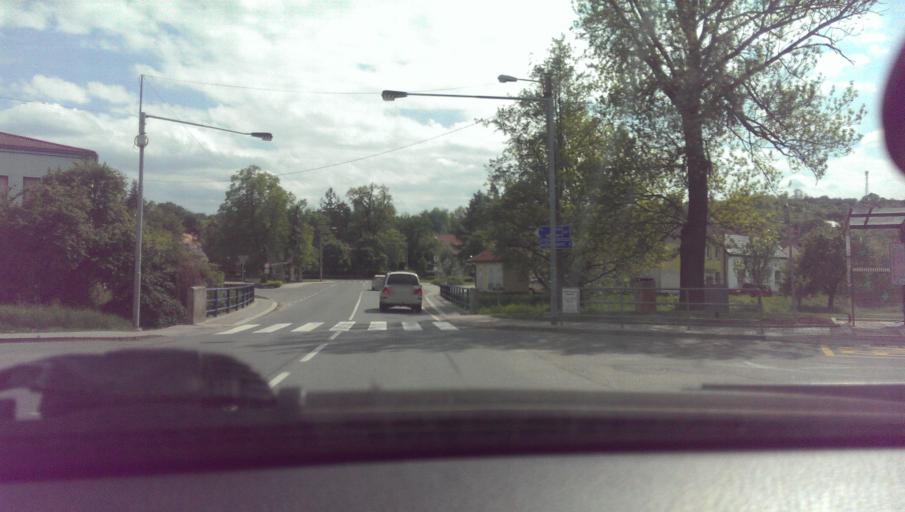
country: CZ
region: Zlin
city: Bilovice
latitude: 49.1001
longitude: 17.5477
